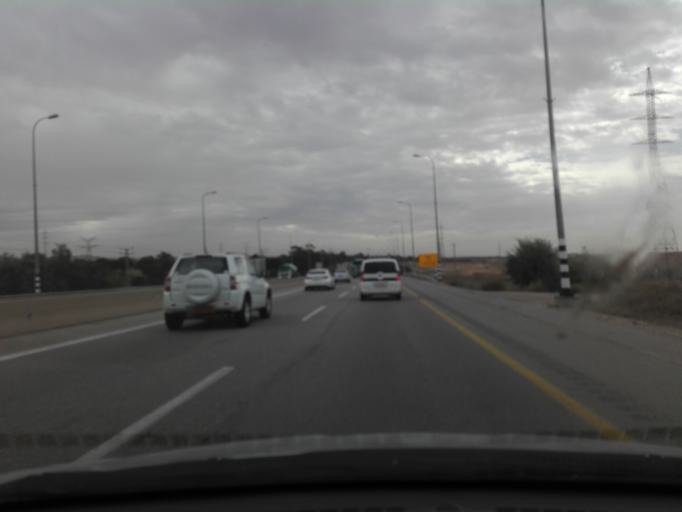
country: IL
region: Southern District
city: Lehavim
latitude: 31.3694
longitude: 34.7945
